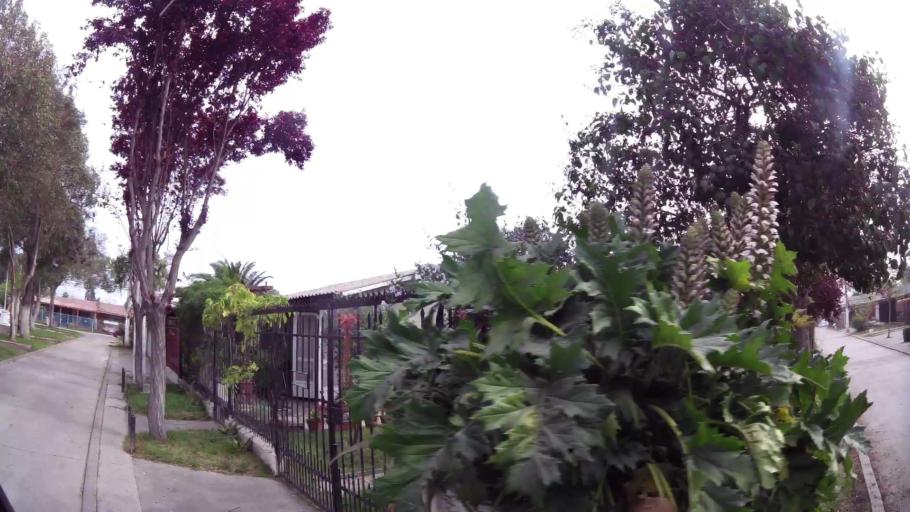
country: CL
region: Santiago Metropolitan
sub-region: Provincia de Santiago
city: Lo Prado
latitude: -33.5190
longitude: -70.7621
